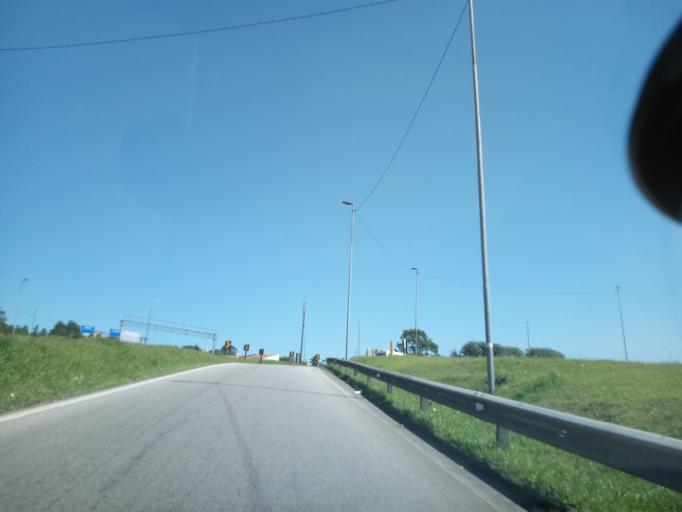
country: BR
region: Sao Paulo
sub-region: Sao Bernardo Do Campo
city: Sao Bernardo do Campo
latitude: -23.7773
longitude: -46.5272
